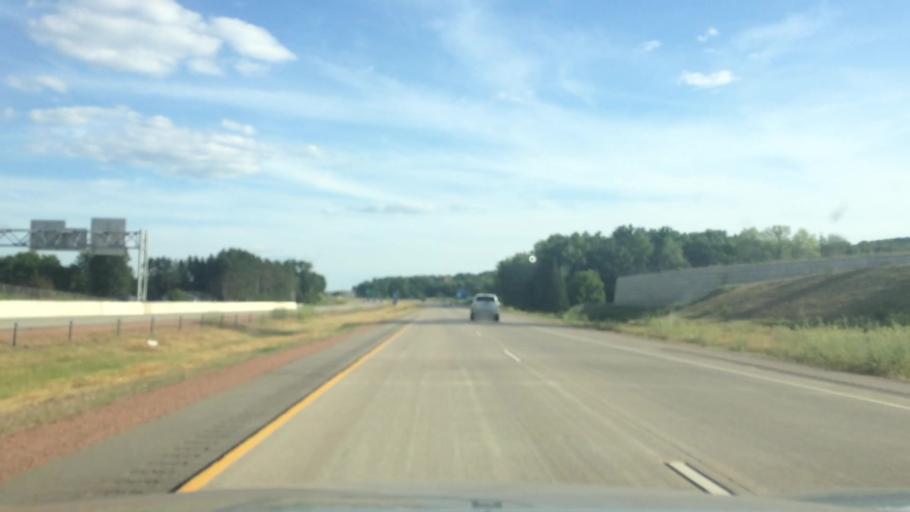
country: US
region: Wisconsin
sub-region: Marathon County
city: Wausau
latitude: 44.9846
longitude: -89.6573
